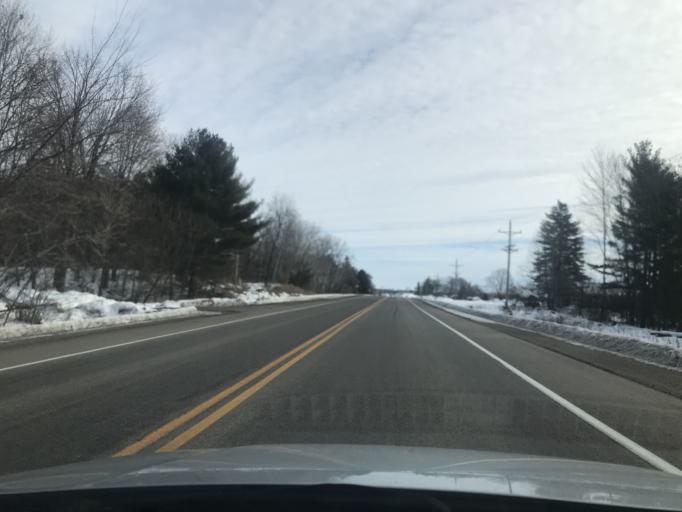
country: US
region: Wisconsin
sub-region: Oconto County
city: Oconto Falls
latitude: 44.8868
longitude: -88.1624
